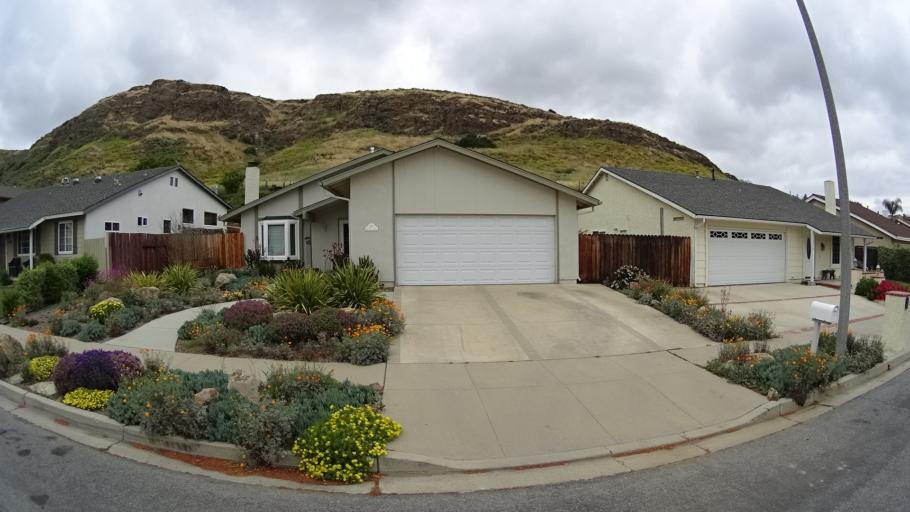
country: US
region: California
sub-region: Ventura County
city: Casa Conejo
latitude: 34.2247
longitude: -118.8983
